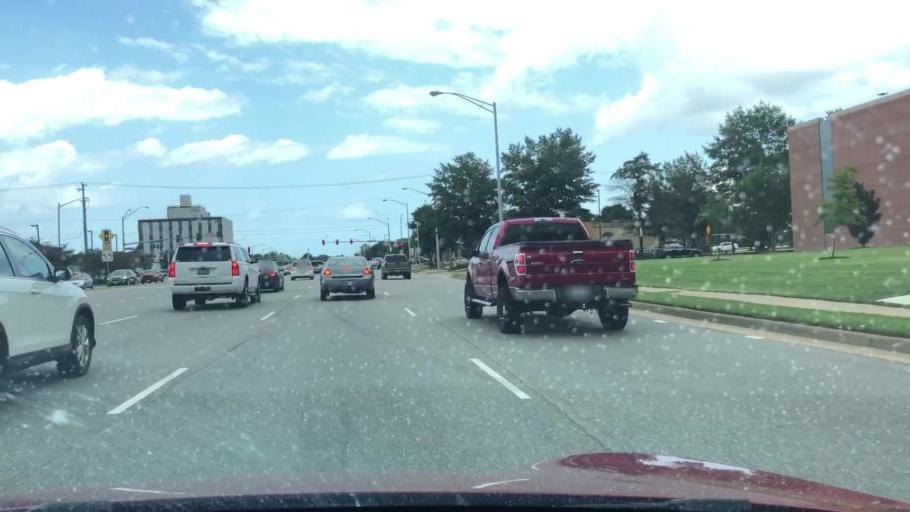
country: US
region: Virginia
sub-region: City of Chesapeake
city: Chesapeake
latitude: 36.8420
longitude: -76.1367
